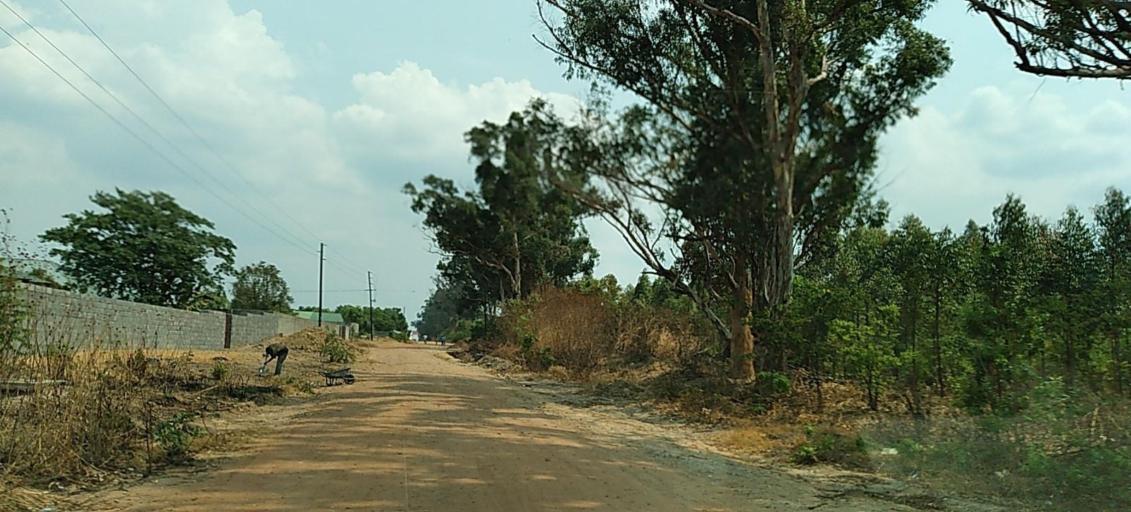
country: ZM
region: Copperbelt
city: Kalulushi
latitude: -12.8397
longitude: 28.0777
